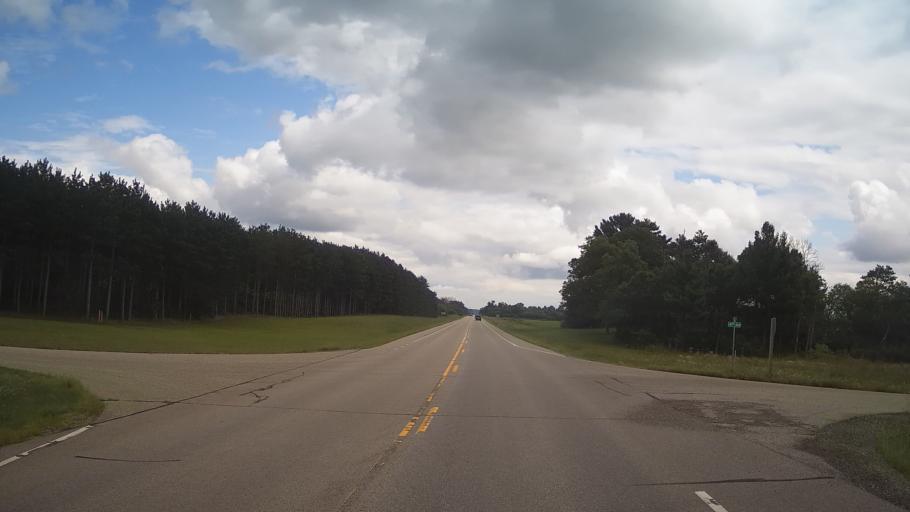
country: US
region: Wisconsin
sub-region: Adams County
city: Friendship
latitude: 44.0219
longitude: -89.6587
